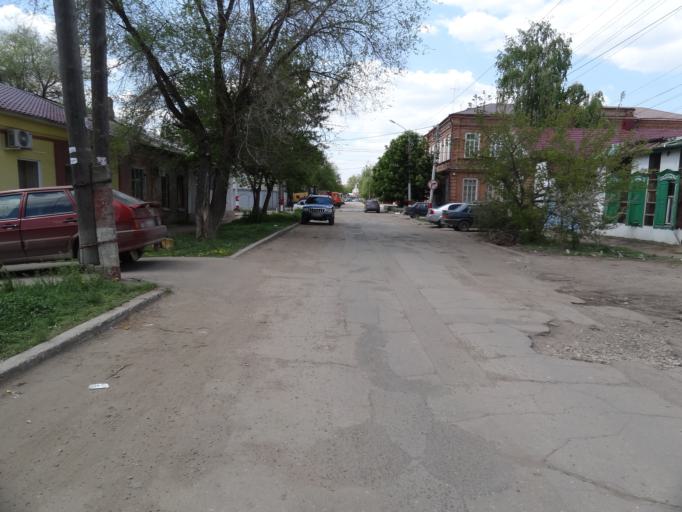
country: RU
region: Saratov
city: Engel's
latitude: 51.4996
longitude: 46.1322
